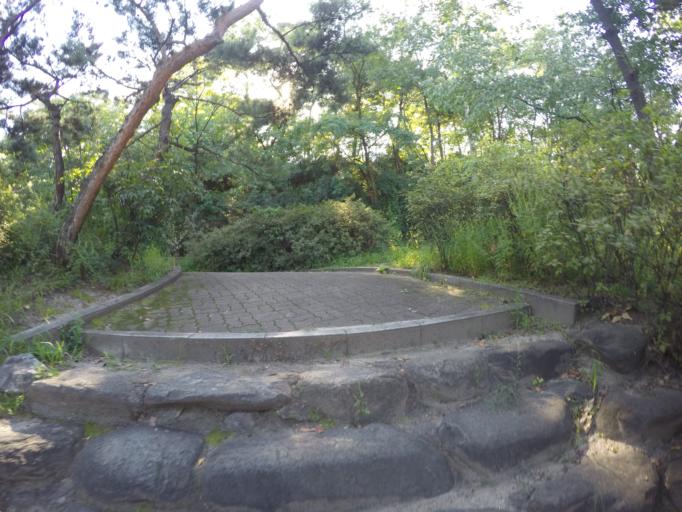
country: KR
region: Seoul
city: Seoul
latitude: 37.5574
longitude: 126.9929
